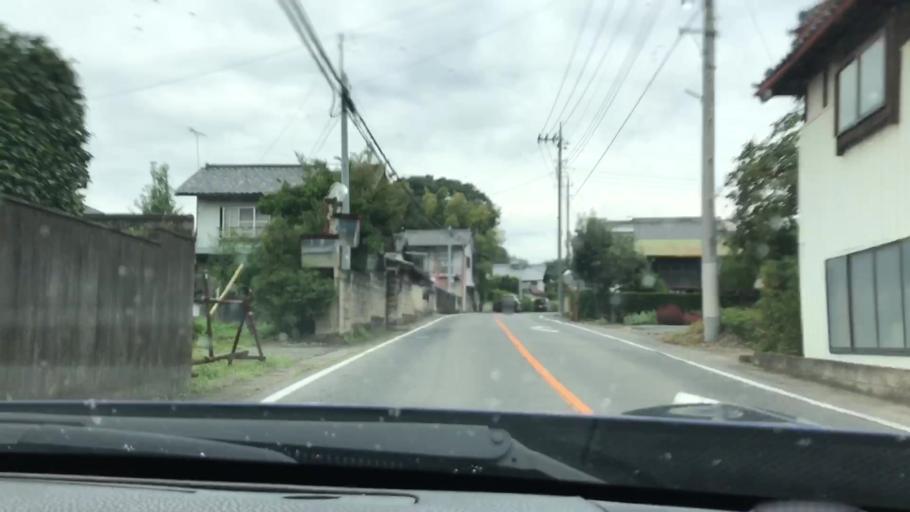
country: JP
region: Gunma
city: Kanekomachi
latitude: 36.3958
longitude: 138.9754
